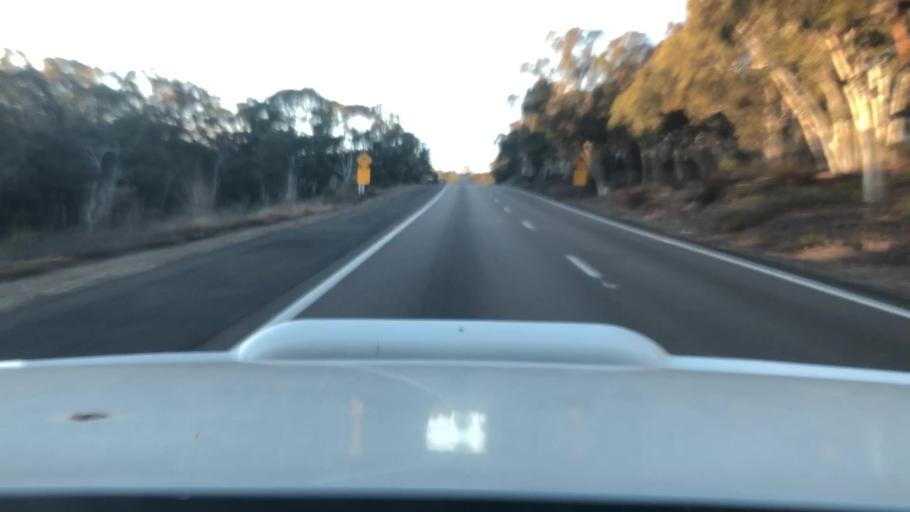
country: AU
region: New South Wales
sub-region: Goulburn Mulwaree
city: Goulburn
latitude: -34.7410
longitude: 149.8388
